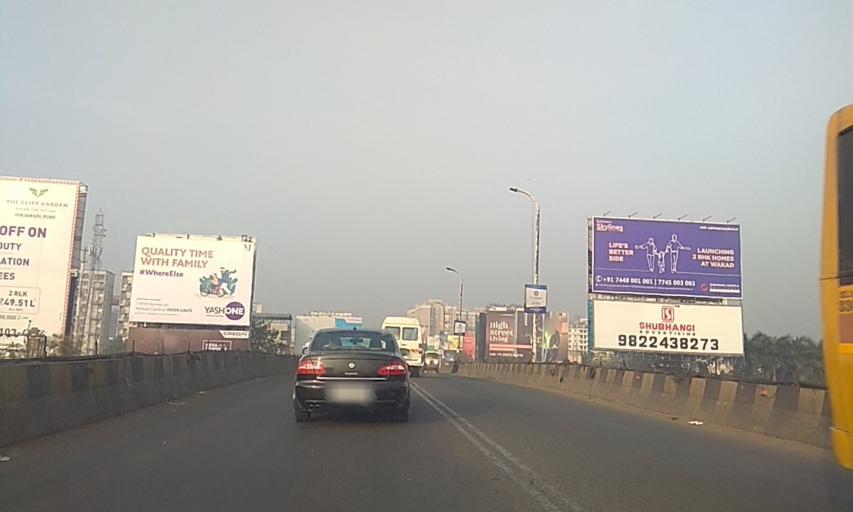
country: IN
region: Maharashtra
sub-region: Pune Division
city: Pimpri
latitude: 18.5920
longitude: 73.7574
